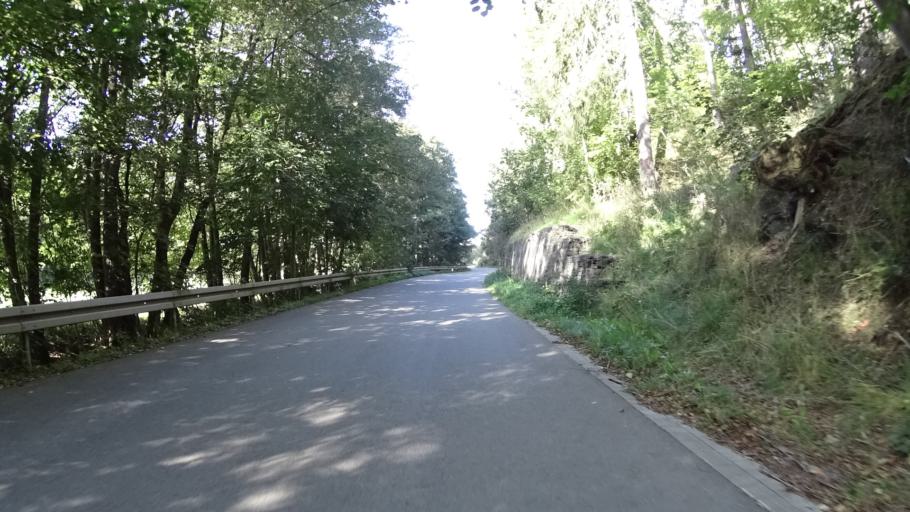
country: DE
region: Thuringia
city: Mohrenbach
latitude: 50.6447
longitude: 10.9852
